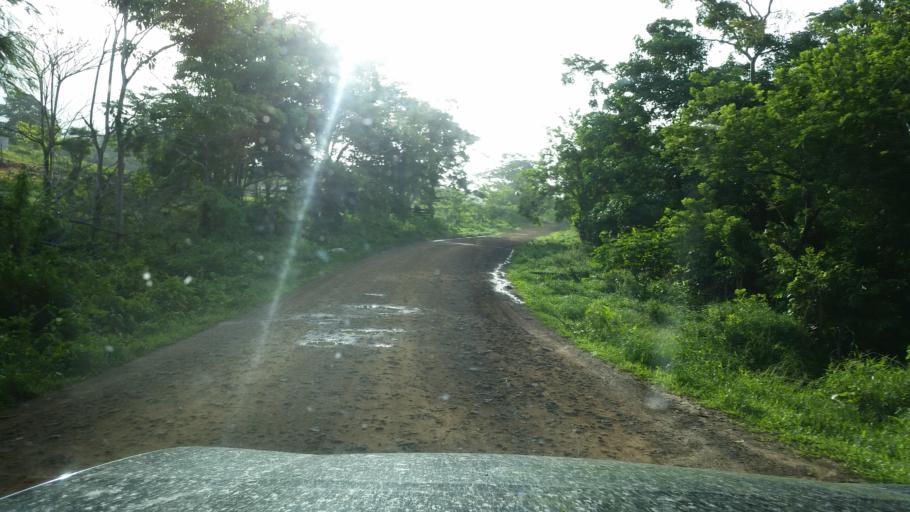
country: NI
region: Atlantico Norte (RAAN)
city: Puerto Cabezas
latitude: 14.0683
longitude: -83.9781
